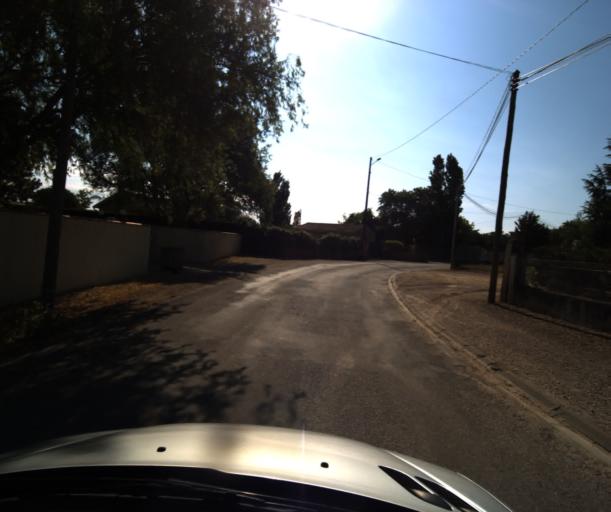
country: FR
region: Midi-Pyrenees
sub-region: Departement du Tarn-et-Garonne
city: Bressols
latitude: 43.9403
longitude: 1.3056
